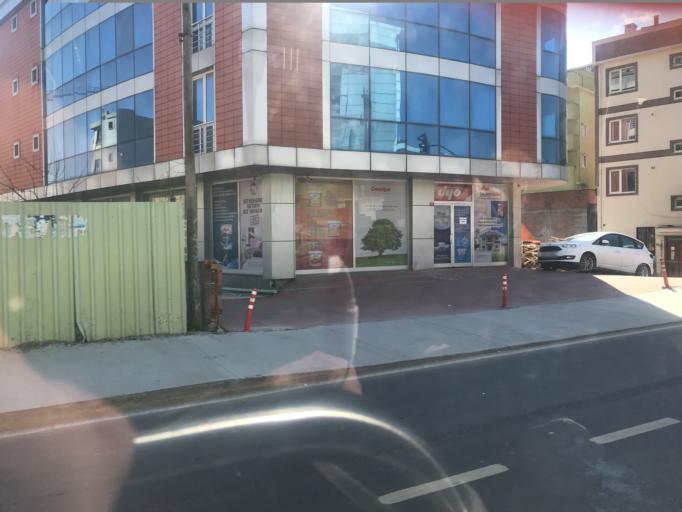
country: TR
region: Istanbul
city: Pendik
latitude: 40.8975
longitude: 29.2544
